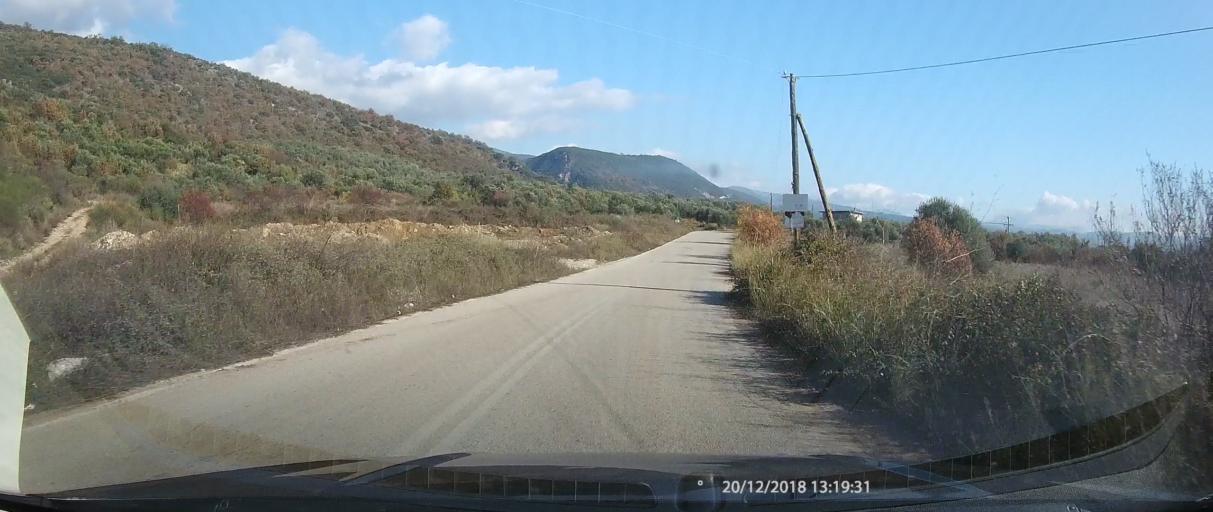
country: GR
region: West Greece
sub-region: Nomos Aitolias kai Akarnanias
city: Paravola
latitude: 38.6140
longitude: 21.5335
